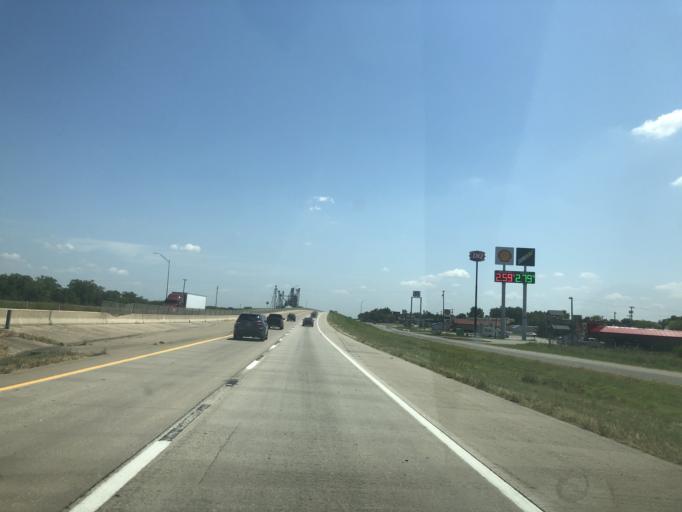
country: US
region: Texas
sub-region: Denton County
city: Sanger
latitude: 33.4918
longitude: -97.1628
